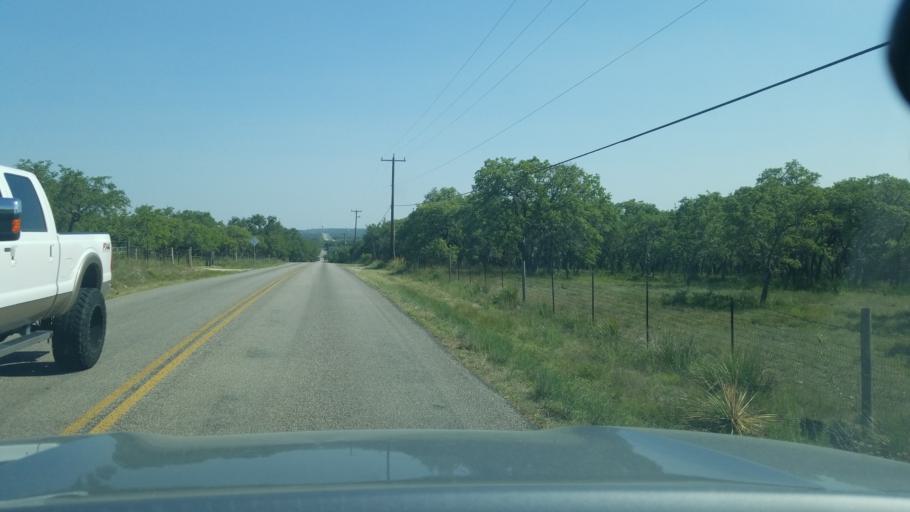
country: US
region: Texas
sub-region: Bexar County
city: Timberwood Park
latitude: 29.7560
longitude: -98.5128
